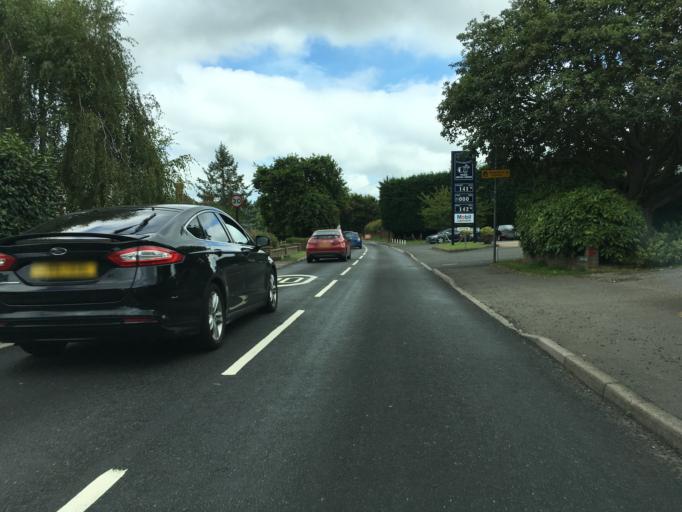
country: GB
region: England
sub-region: Kent
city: Marden
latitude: 51.1143
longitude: 0.4694
